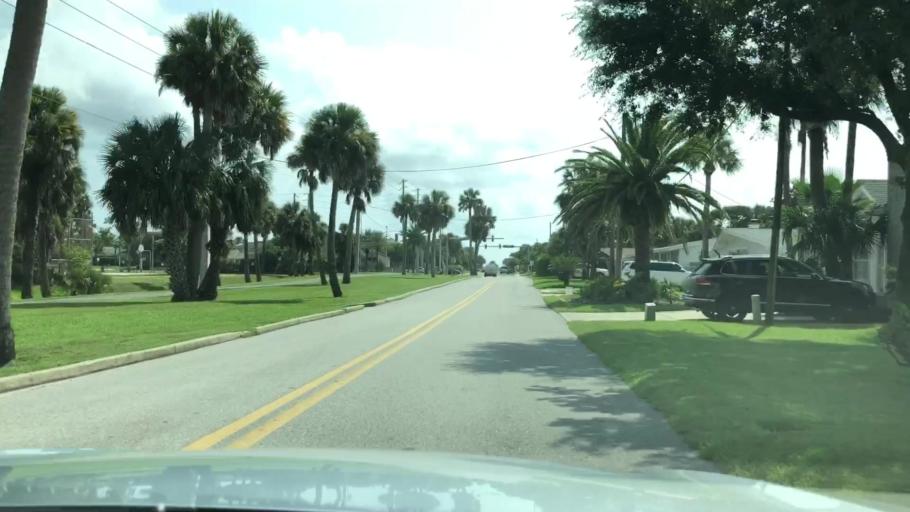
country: US
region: Florida
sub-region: Duval County
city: Neptune Beach
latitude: 30.3143
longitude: -81.3985
